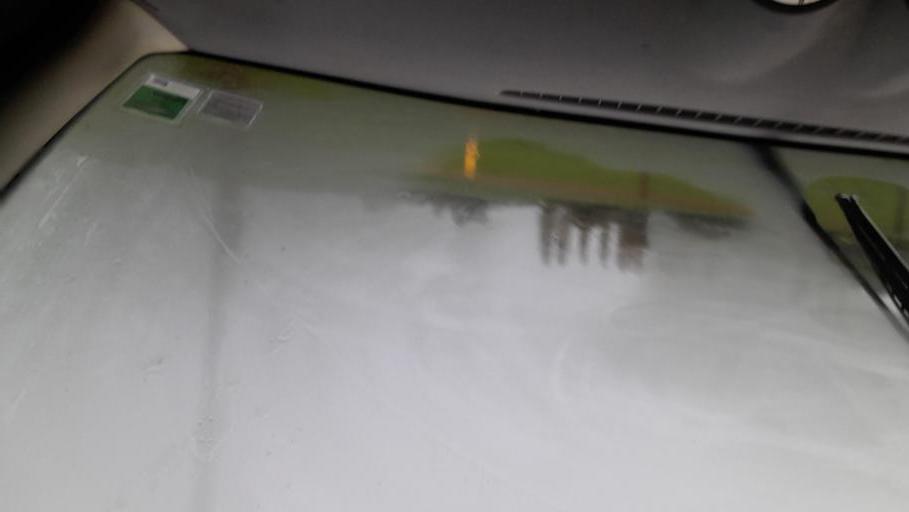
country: FR
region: Pays de la Loire
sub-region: Departement de la Mayenne
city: Ballots
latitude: 47.8566
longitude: -1.0513
